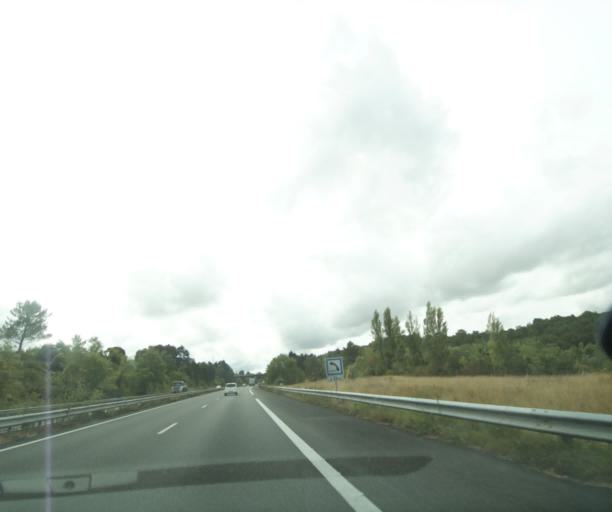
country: FR
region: Poitou-Charentes
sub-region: Departement de la Charente-Maritime
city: Mirambeau
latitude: 45.4086
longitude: -0.6015
